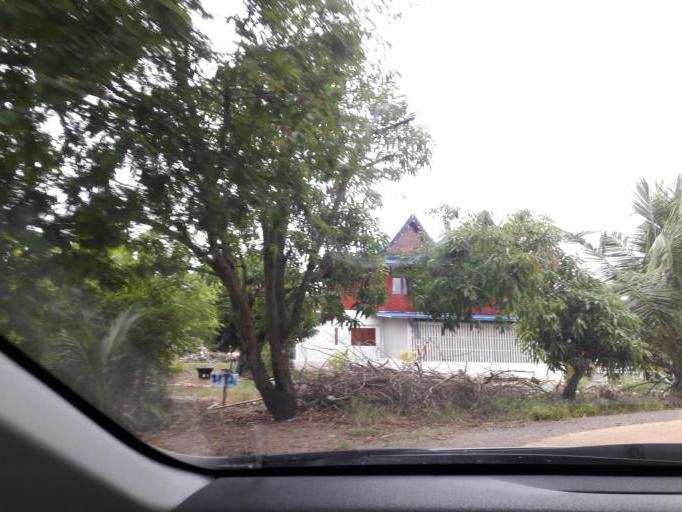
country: TH
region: Samut Sakhon
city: Ban Phaeo
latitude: 13.5863
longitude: 100.0307
